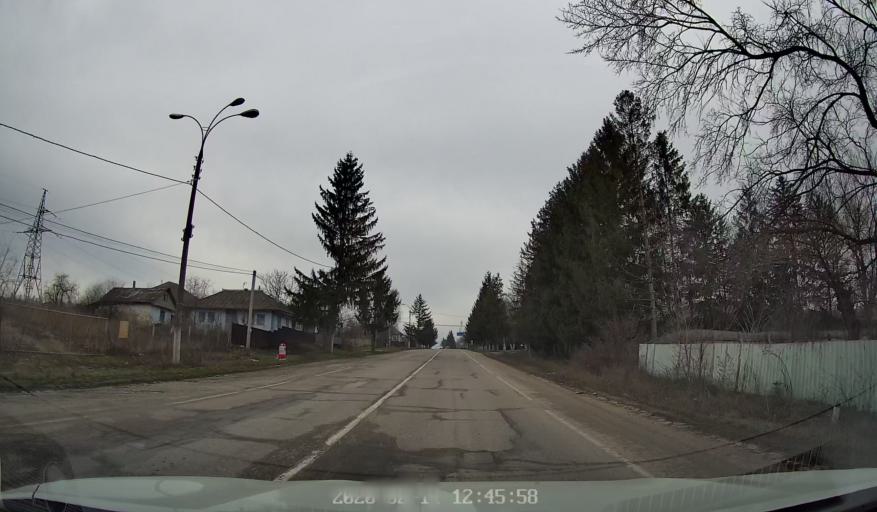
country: MD
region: Raionul Edinet
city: Edinet
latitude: 48.2616
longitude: 27.1864
